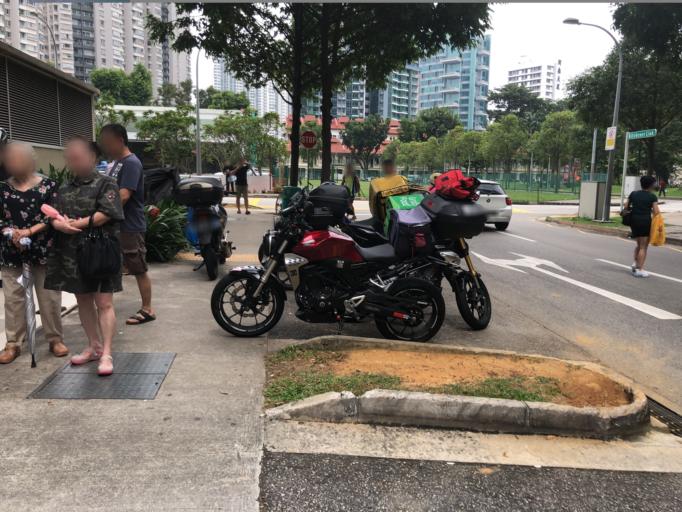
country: SG
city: Singapore
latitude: 1.3113
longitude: 103.8574
